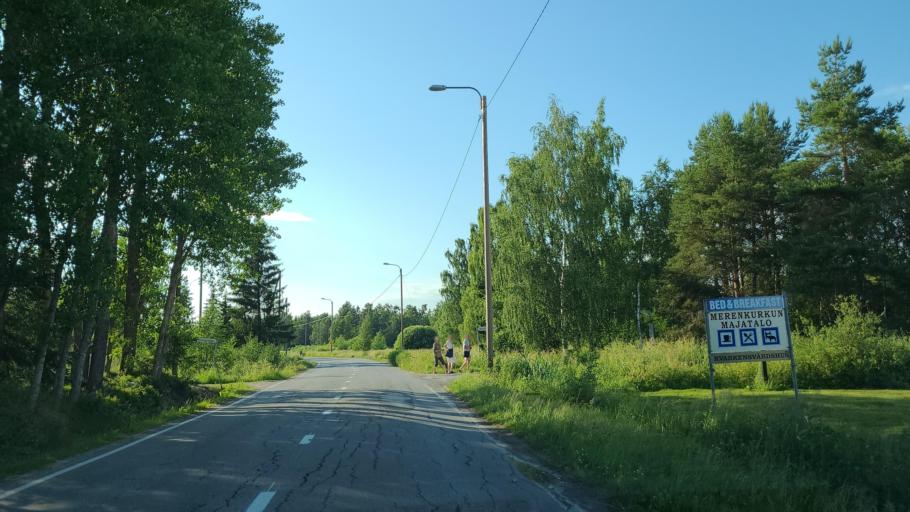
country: FI
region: Ostrobothnia
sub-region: Vaasa
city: Replot
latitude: 63.3484
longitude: 21.3036
